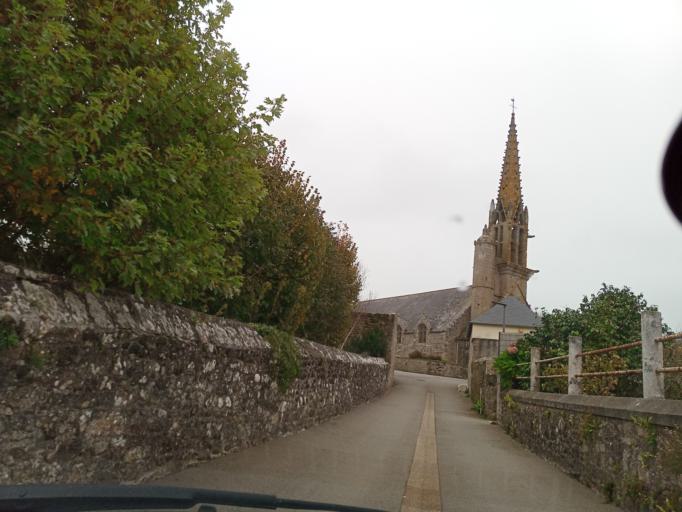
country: FR
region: Brittany
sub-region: Departement du Finistere
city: Esquibien
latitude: 48.0248
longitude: -4.5634
